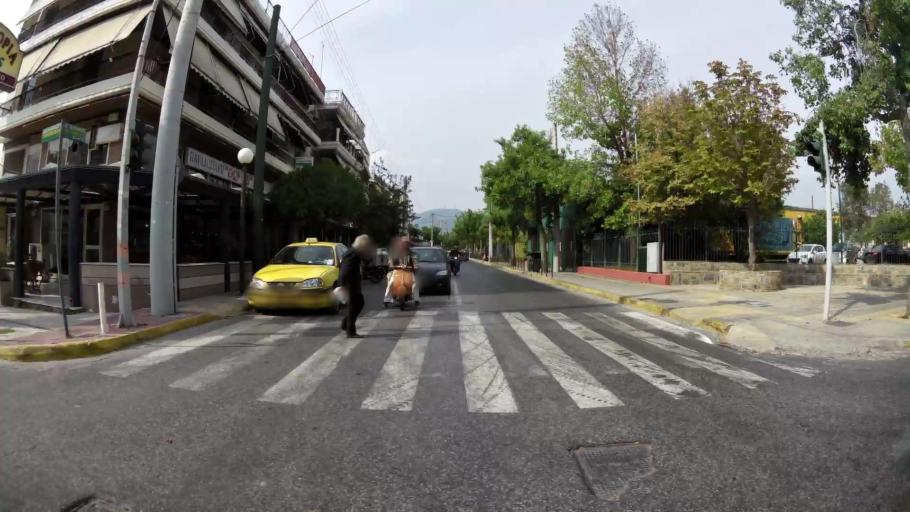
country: GR
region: Attica
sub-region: Nomarchia Athinas
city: Peristeri
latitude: 38.0167
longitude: 23.6887
